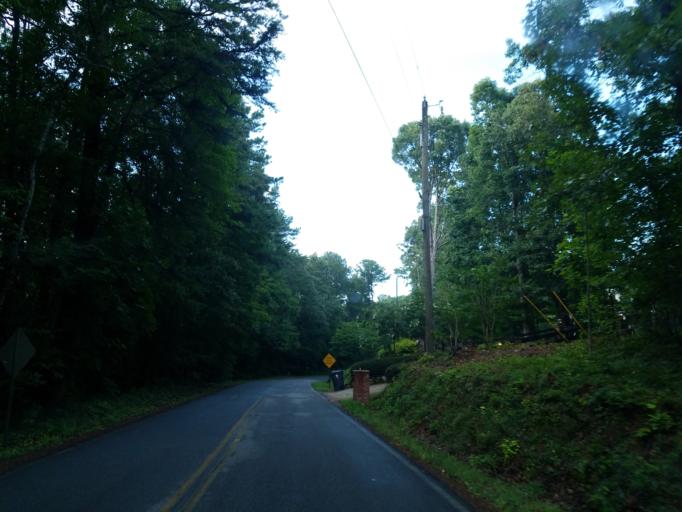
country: US
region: Georgia
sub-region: Bartow County
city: Emerson
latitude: 34.0921
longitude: -84.7649
